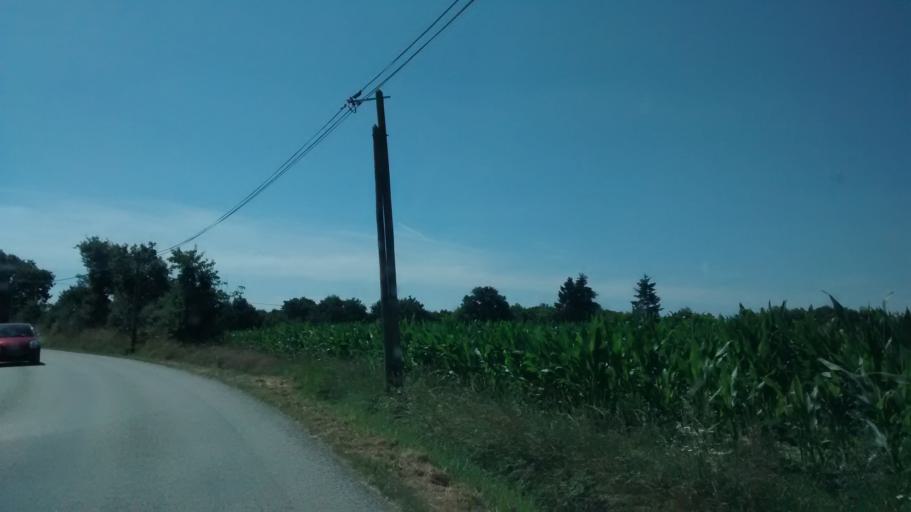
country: FR
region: Brittany
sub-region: Departement du Morbihan
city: Campeneac
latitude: 47.9648
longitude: -2.3042
